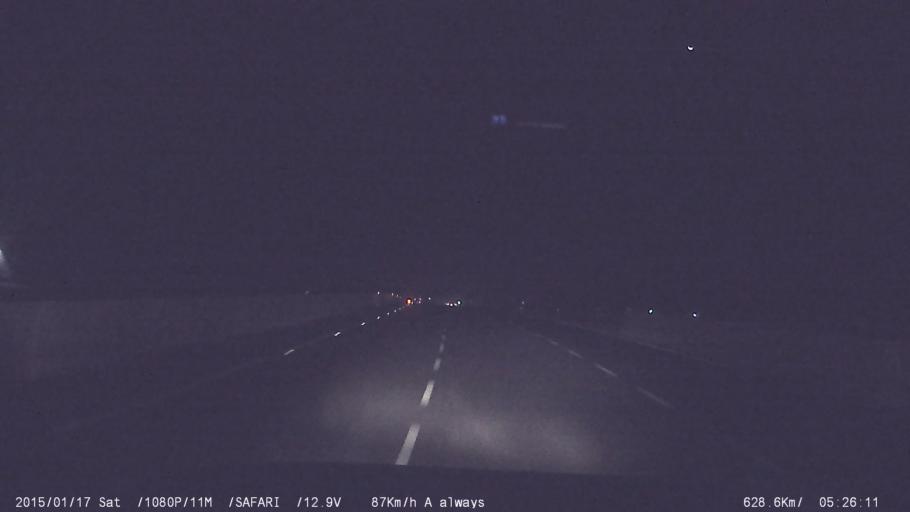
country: IN
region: Tamil Nadu
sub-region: Vellore
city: Arcot
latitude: 12.9385
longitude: 79.2429
